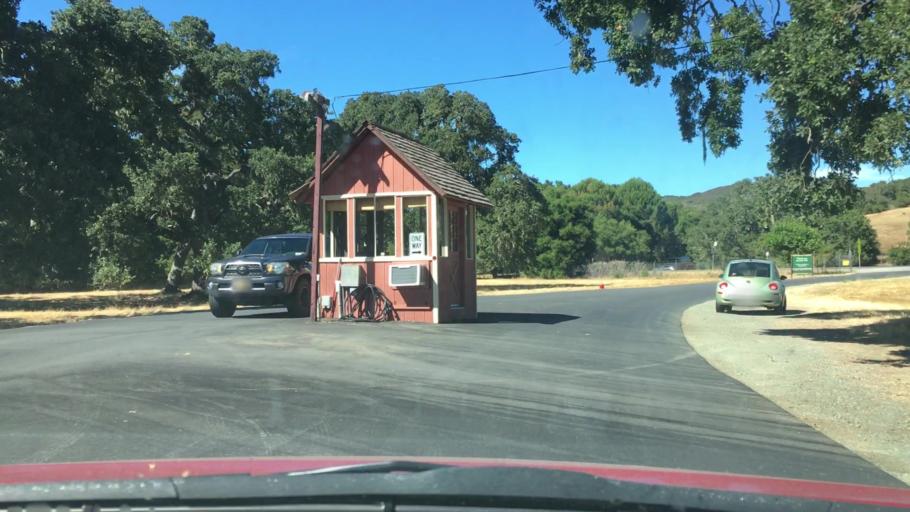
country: US
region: California
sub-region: San Mateo County
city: Emerald Lake Hills
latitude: 37.4780
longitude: -122.3120
